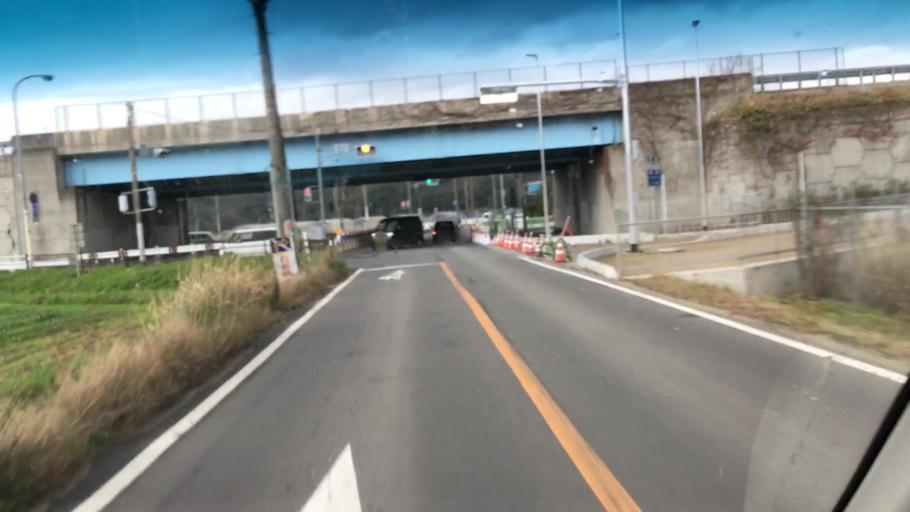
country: JP
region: Fukuoka
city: Maebaru-chuo
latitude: 33.5311
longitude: 130.1880
